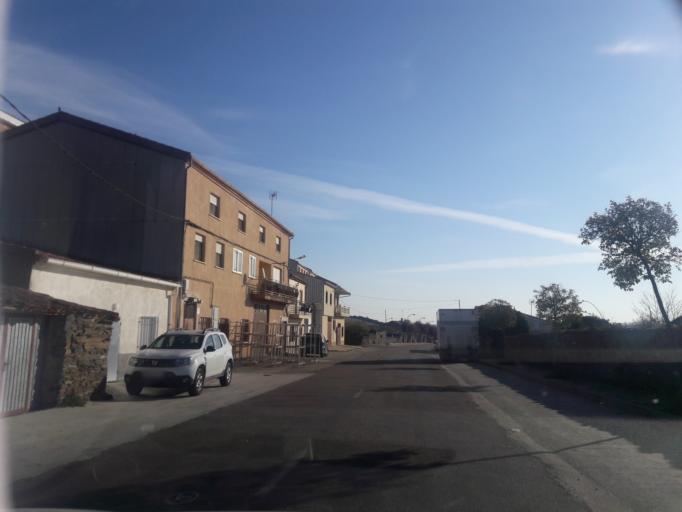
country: ES
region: Castille and Leon
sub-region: Provincia de Salamanca
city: Aldeavieja de Tormes
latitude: 40.5821
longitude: -5.6166
